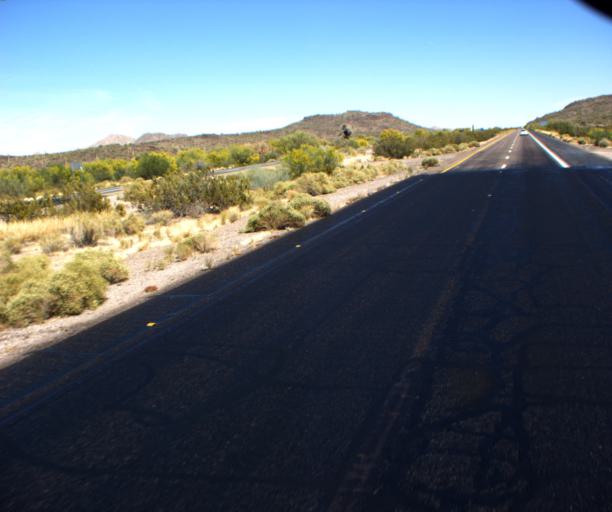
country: US
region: Arizona
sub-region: Pinal County
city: Maricopa
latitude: 32.8362
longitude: -112.2042
